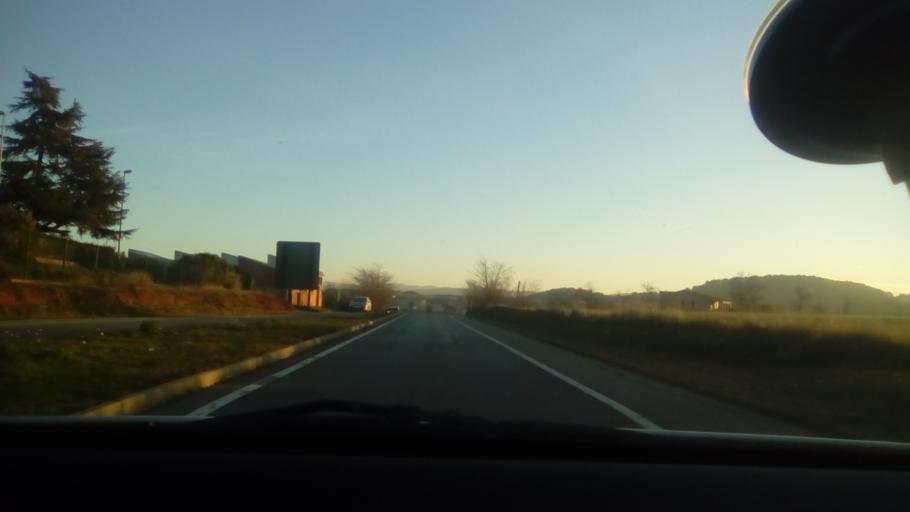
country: ES
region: Catalonia
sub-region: Provincia de Barcelona
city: Sant Fruitos de Bages
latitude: 41.7468
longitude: 1.8628
